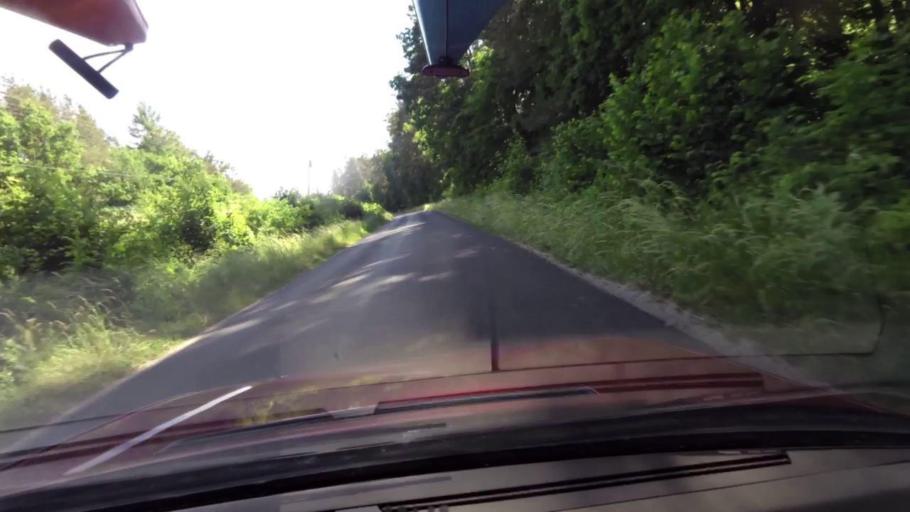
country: PL
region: Pomeranian Voivodeship
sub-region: Powiat slupski
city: Kepice
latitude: 54.2131
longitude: 16.8954
